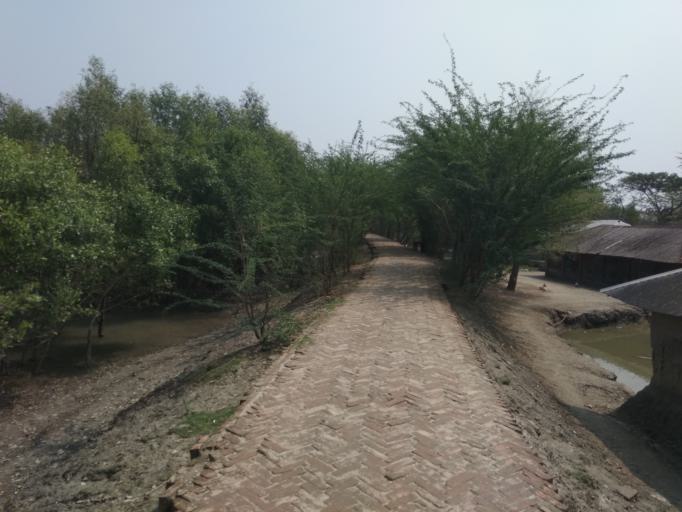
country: IN
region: West Bengal
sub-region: North 24 Parganas
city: Taki
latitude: 22.2814
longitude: 89.2846
